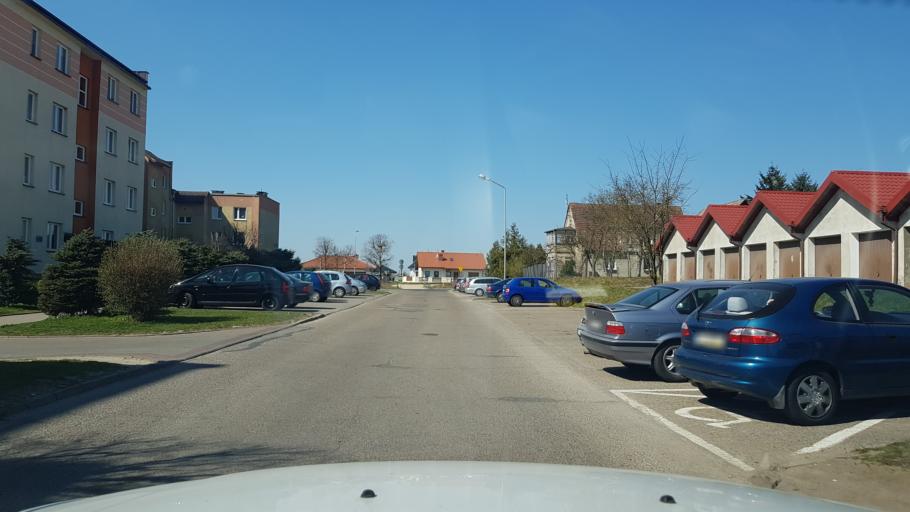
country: PL
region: West Pomeranian Voivodeship
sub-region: Powiat slawienski
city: Slawno
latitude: 54.3716
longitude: 16.6820
